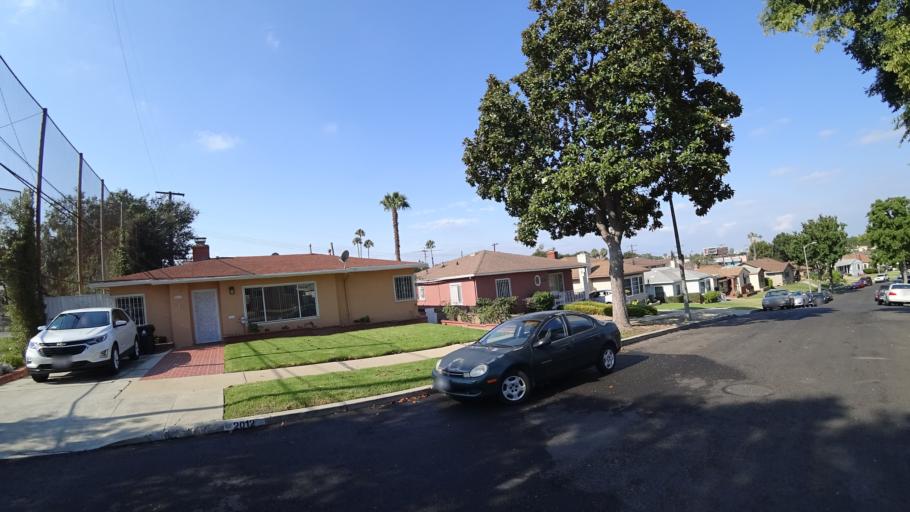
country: US
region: California
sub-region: Los Angeles County
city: Westmont
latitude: 33.9463
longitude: -118.3141
